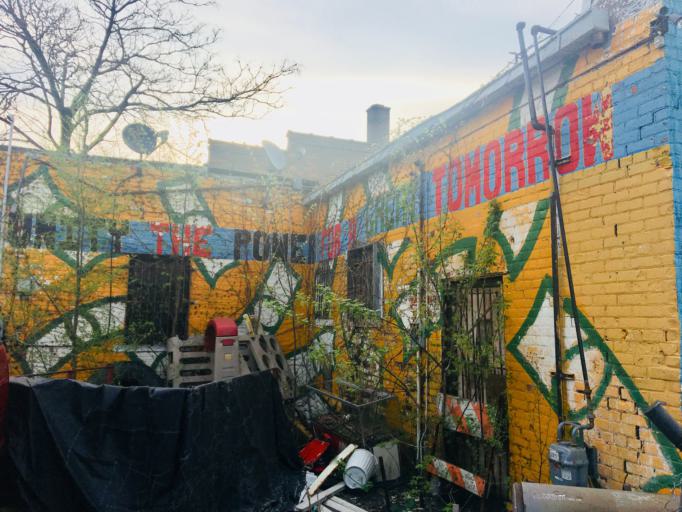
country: US
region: Michigan
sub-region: Wayne County
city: Grosse Pointe Park
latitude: 42.4034
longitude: -82.9703
